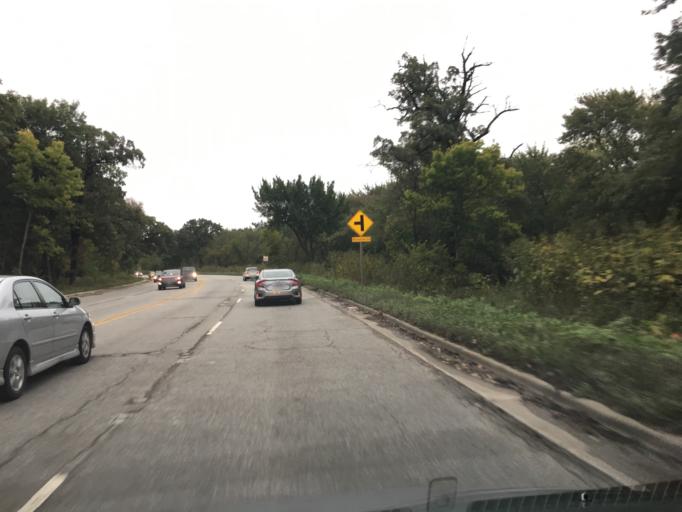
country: US
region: Illinois
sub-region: Cook County
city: Lyons
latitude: 41.8211
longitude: -87.8308
